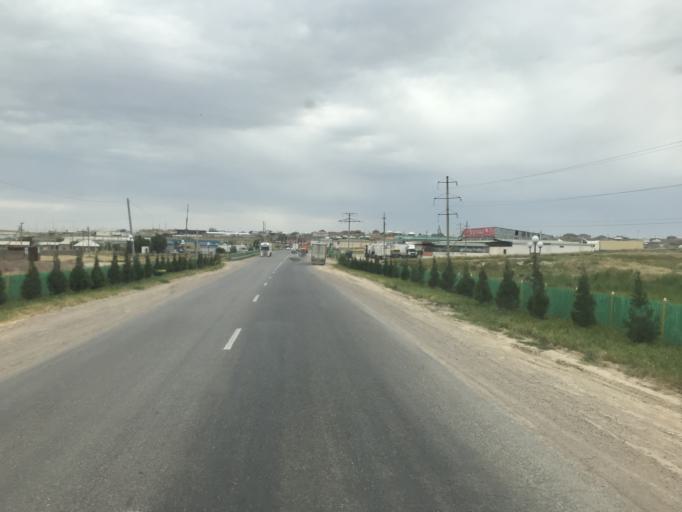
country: KZ
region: Ongtustik Qazaqstan
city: Saryaghash
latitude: 41.4762
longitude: 69.2101
